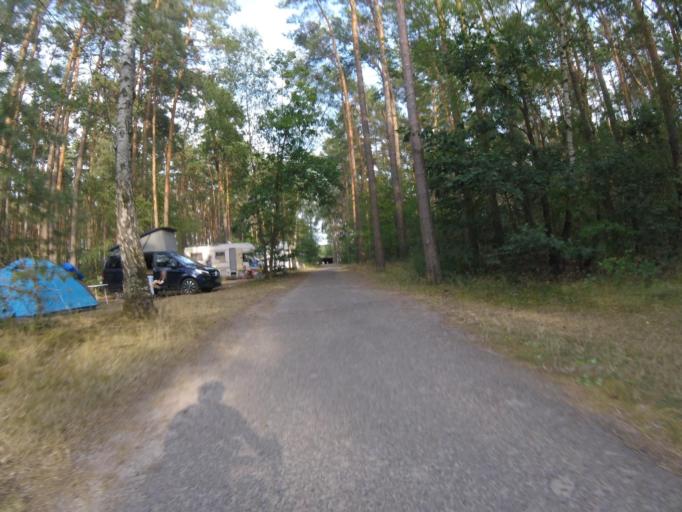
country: DE
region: Brandenburg
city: Gross Koris
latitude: 52.2123
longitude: 13.7446
